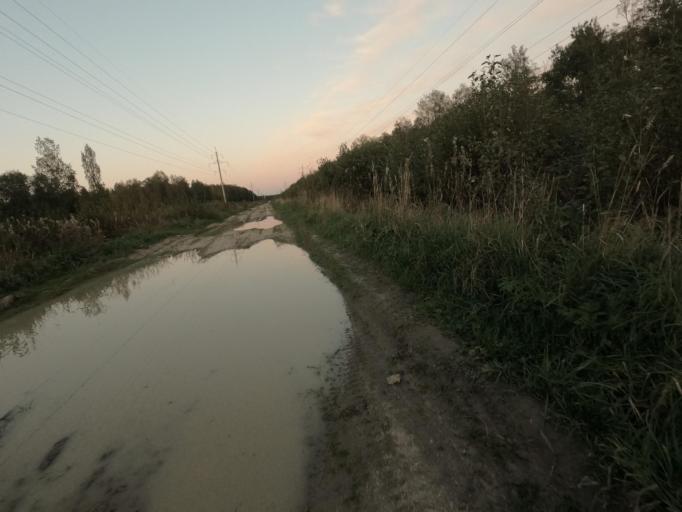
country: RU
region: Leningrad
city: Otradnoye
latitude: 59.7703
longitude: 30.8478
